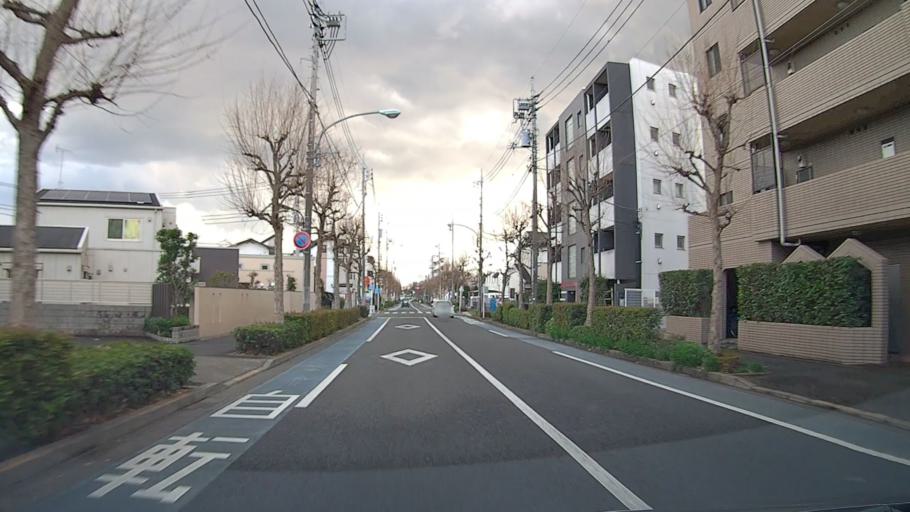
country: JP
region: Saitama
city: Wako
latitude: 35.7499
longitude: 139.6449
